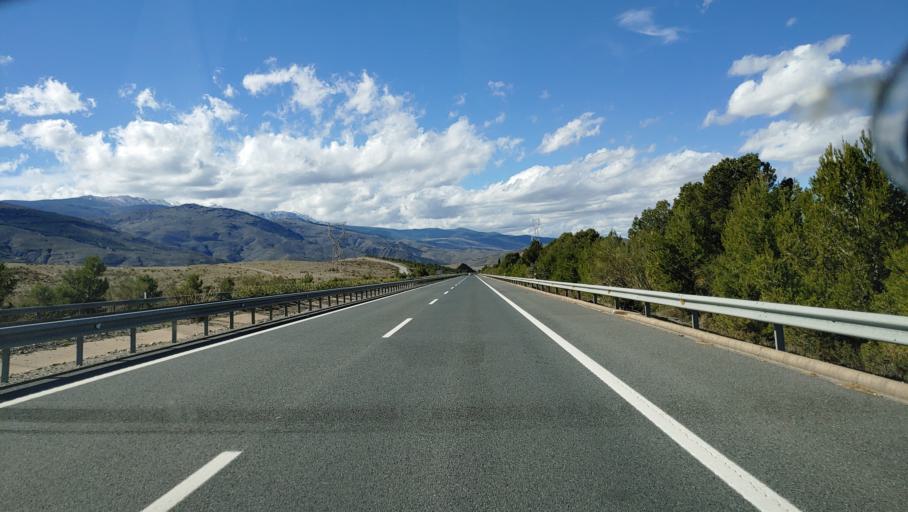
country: ES
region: Andalusia
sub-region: Provincia de Almeria
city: Abla
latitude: 37.1386
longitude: -2.6805
